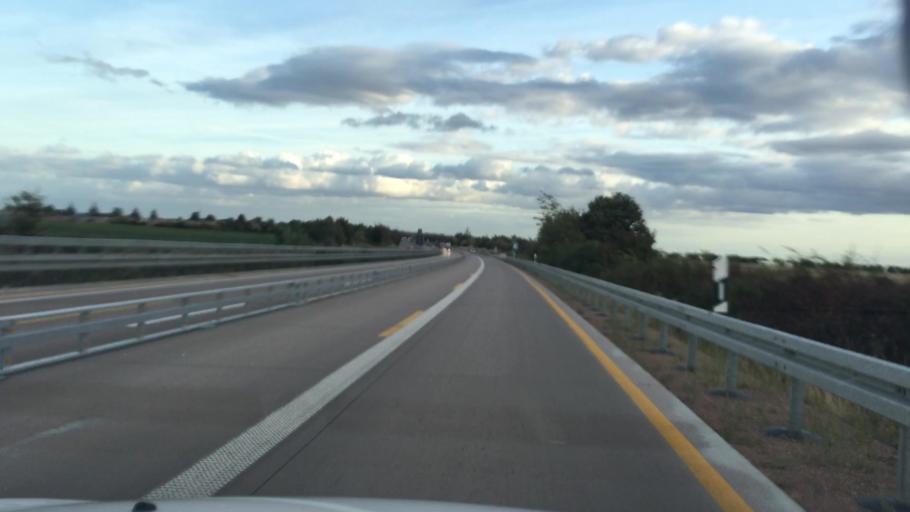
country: DE
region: Saxony-Anhalt
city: Nauendorf
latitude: 51.5943
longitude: 11.8728
